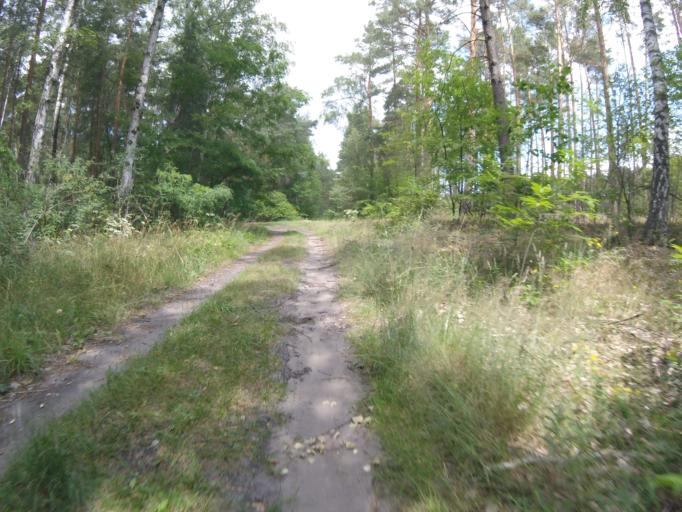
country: DE
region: Brandenburg
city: Gross Koris
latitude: 52.1978
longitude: 13.6477
